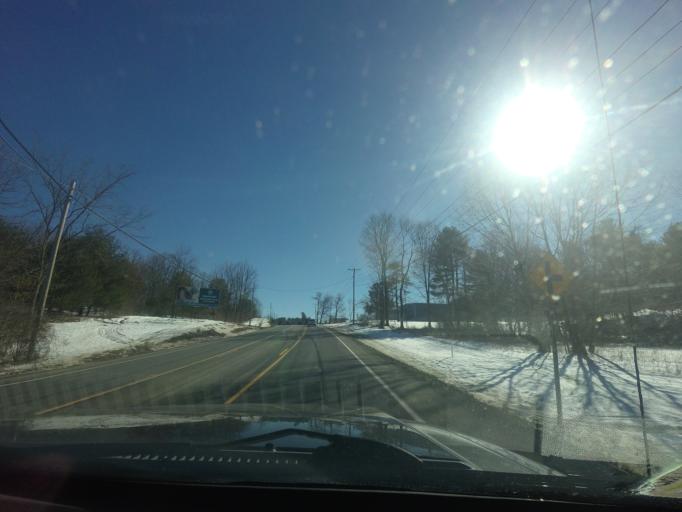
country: US
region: New York
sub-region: Rensselaer County
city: East Greenbush
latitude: 42.5427
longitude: -73.6661
